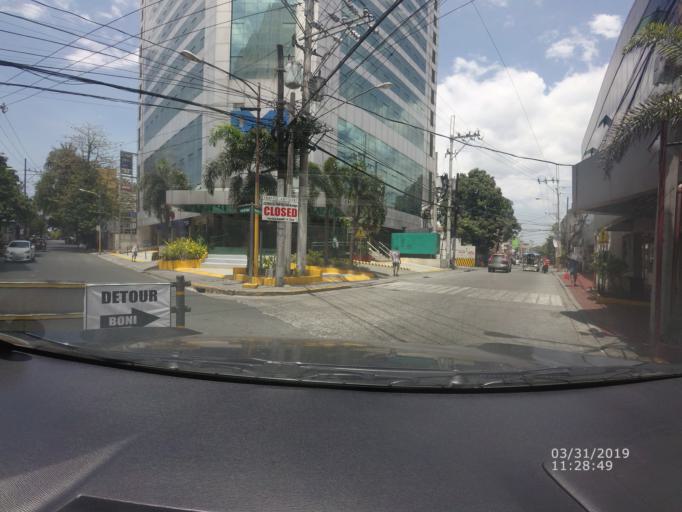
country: PH
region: Metro Manila
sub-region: Mandaluyong
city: Mandaluyong City
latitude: 14.5795
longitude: 121.0457
